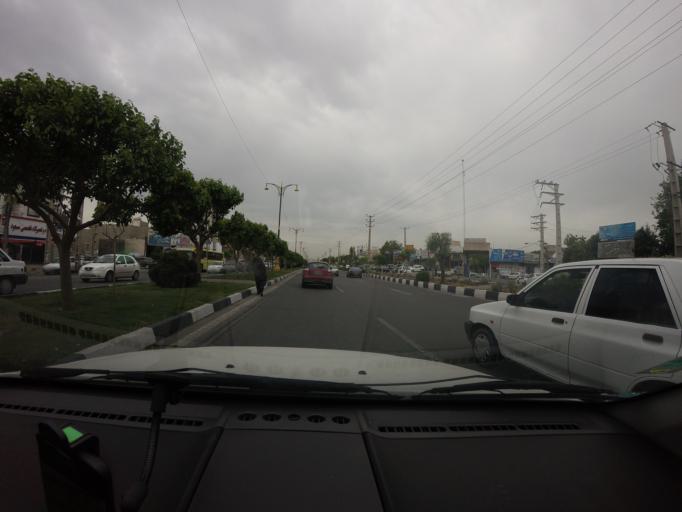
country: IR
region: Tehran
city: Eslamshahr
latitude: 35.5468
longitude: 51.2224
